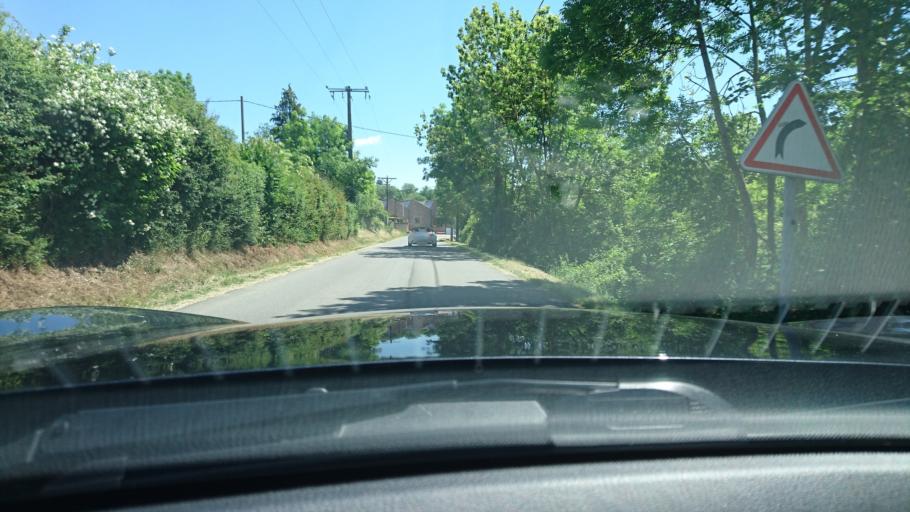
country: FR
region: Rhone-Alpes
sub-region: Departement de la Loire
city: Panissieres
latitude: 45.7960
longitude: 4.3431
